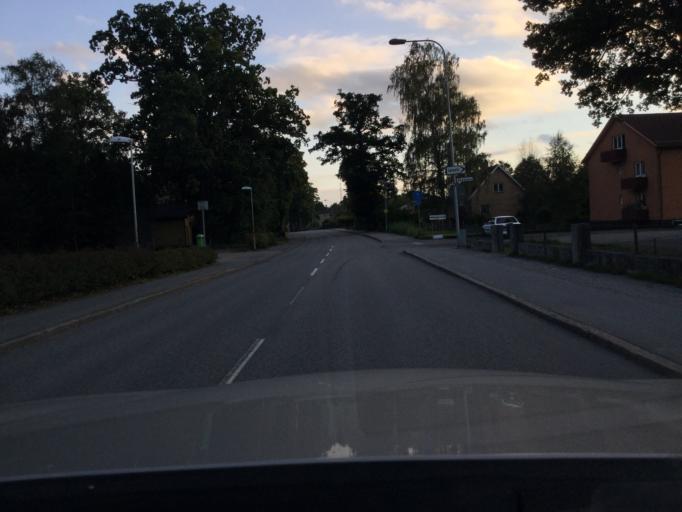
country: SE
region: Kronoberg
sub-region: Almhults Kommun
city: AElmhult
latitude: 56.6391
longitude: 14.2217
